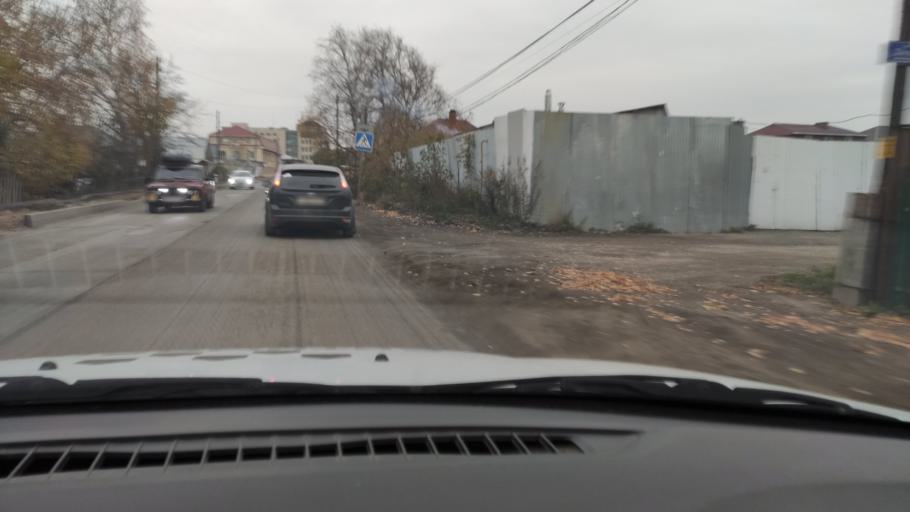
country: RU
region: Perm
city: Kondratovo
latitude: 57.9602
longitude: 56.1262
